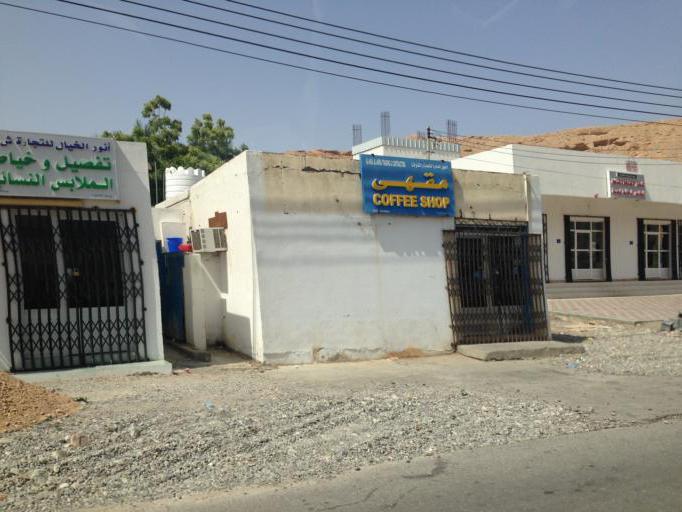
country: OM
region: Ash Sharqiyah
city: Ibra'
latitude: 23.0924
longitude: 58.8610
